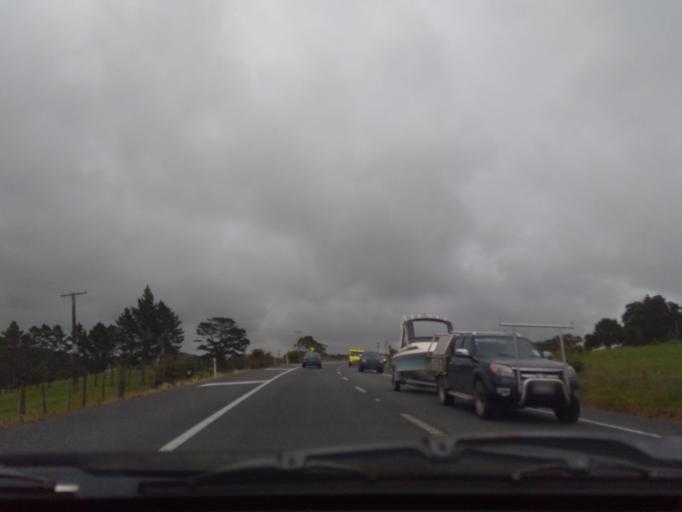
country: NZ
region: Northland
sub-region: Whangarei
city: Ruakaka
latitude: -35.8519
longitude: 174.3562
